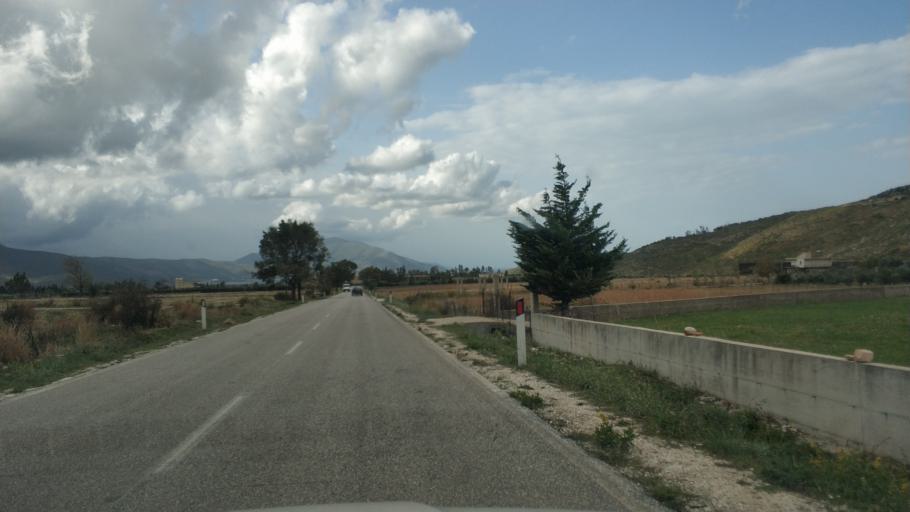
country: AL
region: Vlore
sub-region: Rrethi i Vlores
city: Orikum
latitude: 40.2755
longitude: 19.5077
